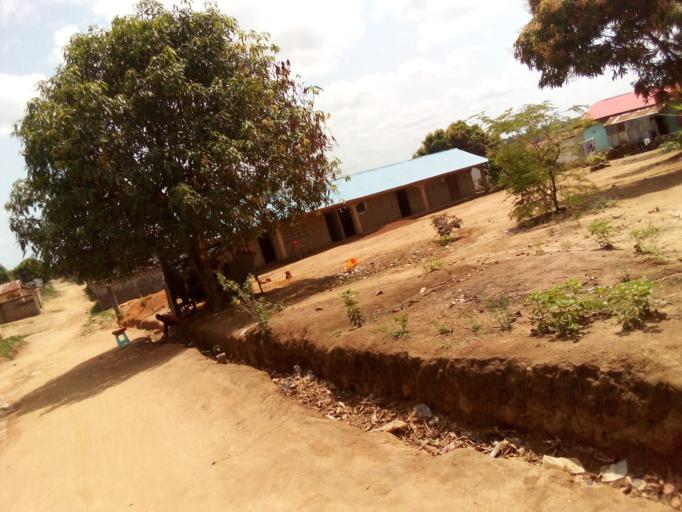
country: SL
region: Western Area
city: Waterloo
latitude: 8.3381
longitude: -13.0232
